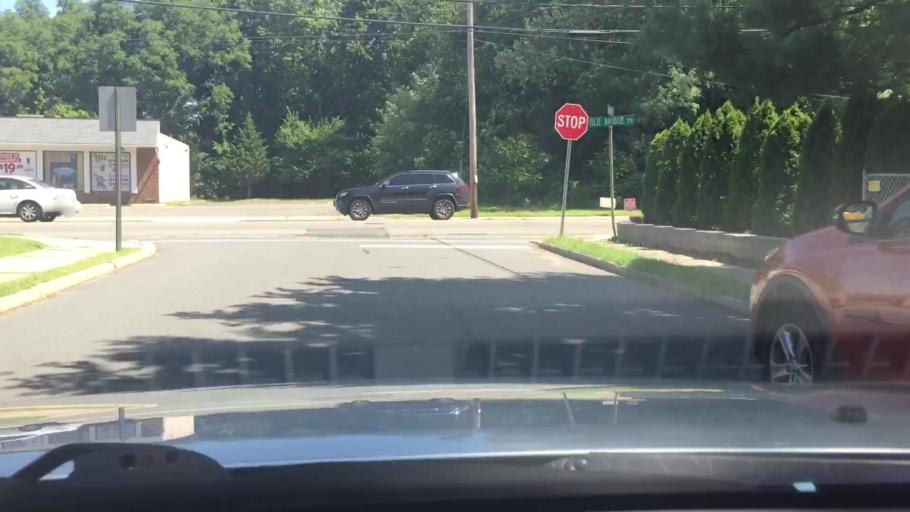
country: US
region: New Jersey
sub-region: Middlesex County
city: South River
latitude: 40.4547
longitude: -74.3937
